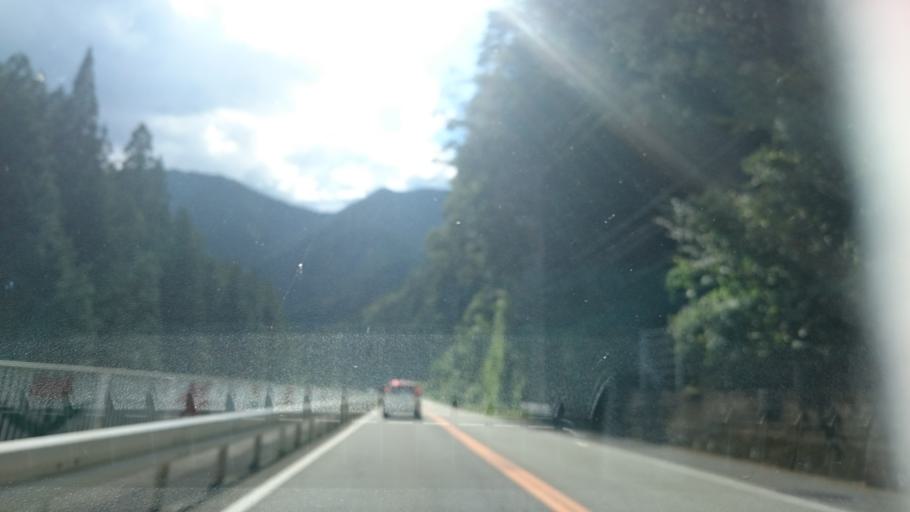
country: JP
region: Gifu
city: Gujo
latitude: 35.7701
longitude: 137.2647
